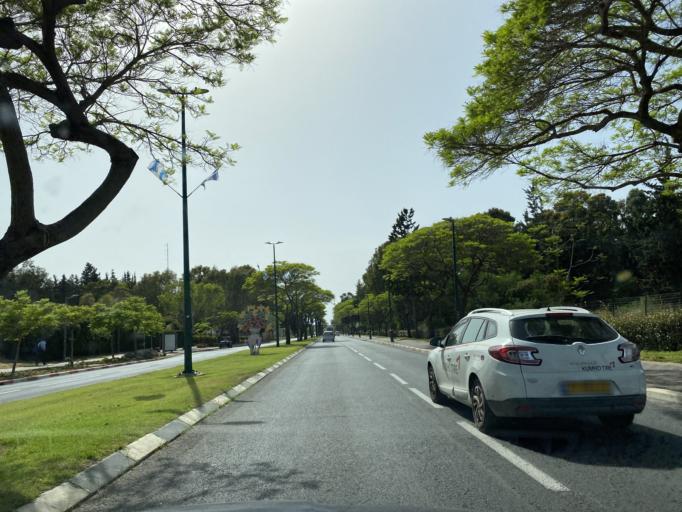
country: IL
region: Tel Aviv
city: Herzliyya
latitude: 32.1776
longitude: 34.8380
